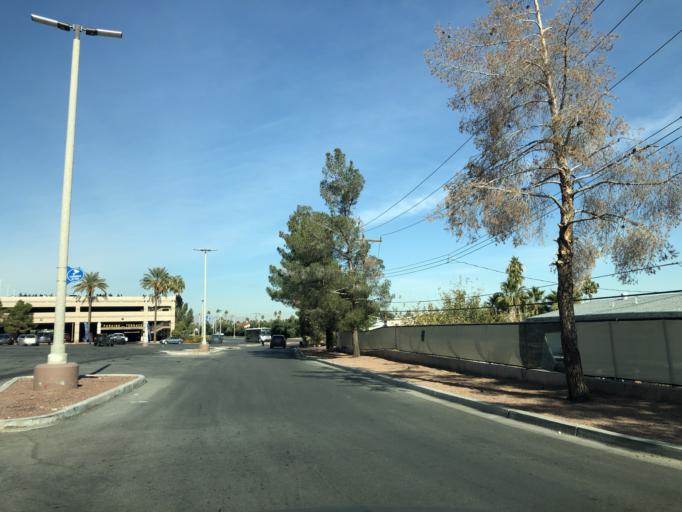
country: US
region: Nevada
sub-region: Clark County
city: Winchester
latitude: 36.1232
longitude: -115.1338
